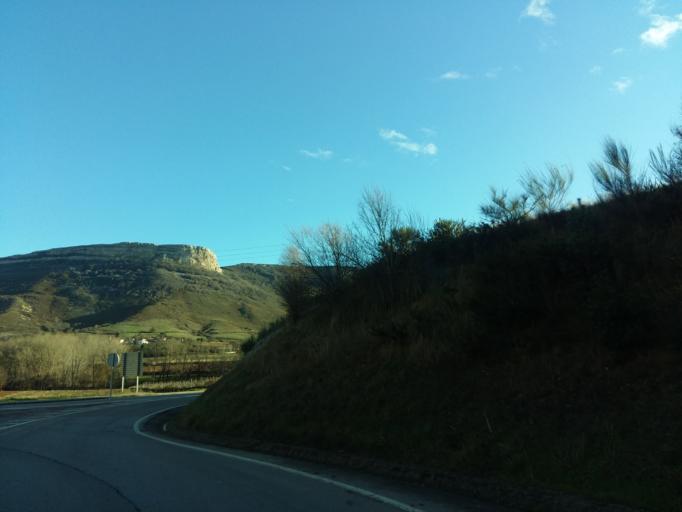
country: ES
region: Cantabria
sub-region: Provincia de Cantabria
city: San Martin de Elines
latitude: 42.8300
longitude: -3.9038
